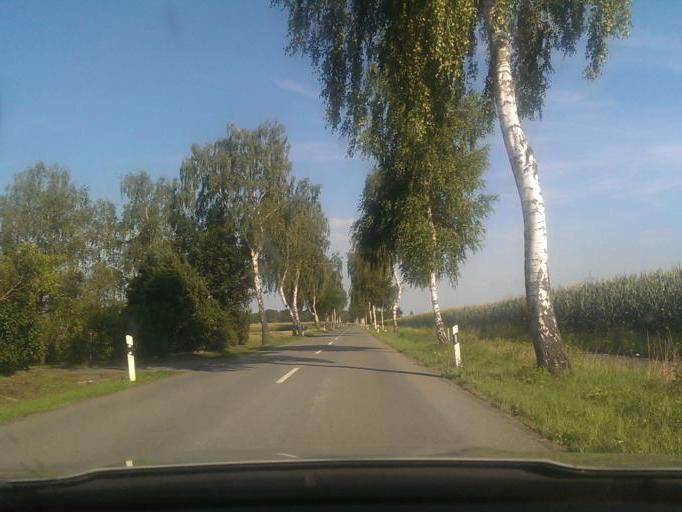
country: DE
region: North Rhine-Westphalia
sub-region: Regierungsbezirk Detmold
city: Delbruck
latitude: 51.7369
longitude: 8.6046
